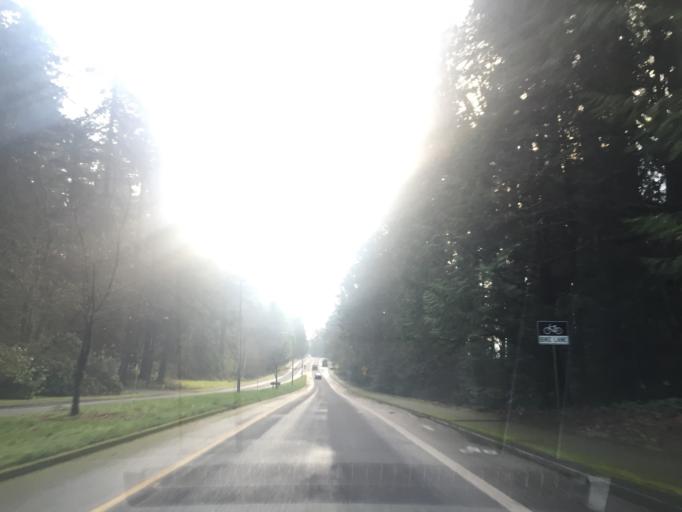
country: US
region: Washington
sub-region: Thurston County
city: Olympia
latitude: 47.0688
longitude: -122.8951
